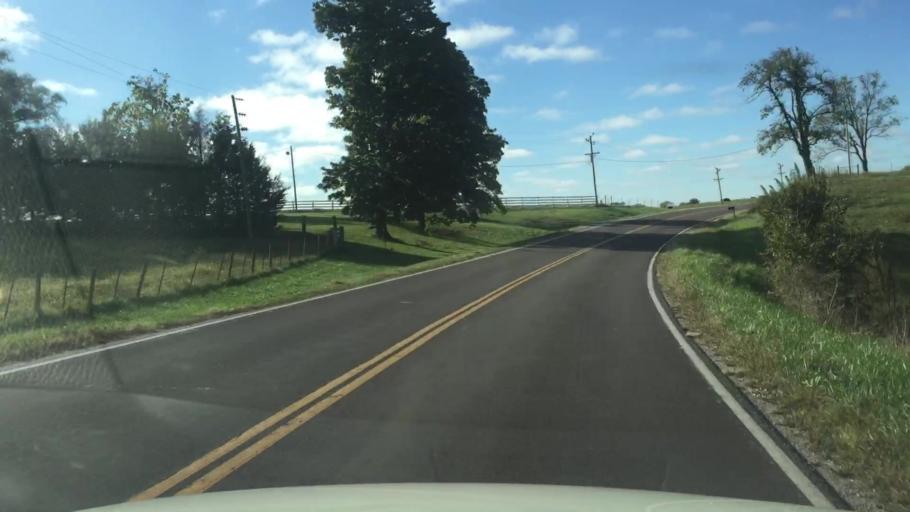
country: US
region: Missouri
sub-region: Howard County
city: New Franklin
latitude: 39.0899
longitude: -92.7434
